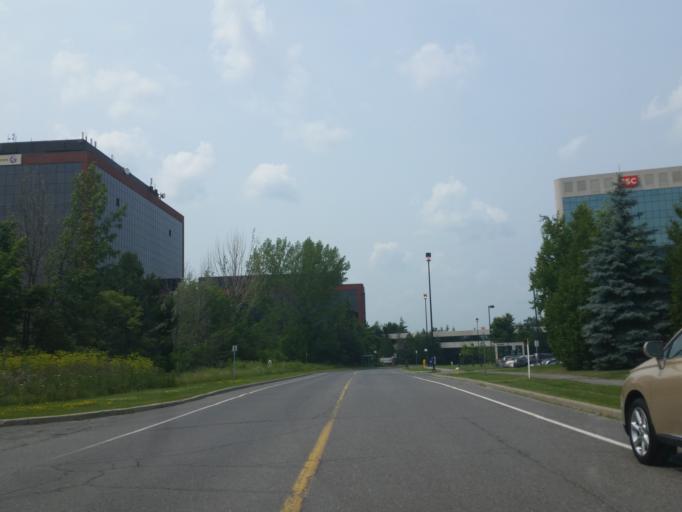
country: CA
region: Ontario
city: Bells Corners
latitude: 45.3474
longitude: -75.9193
